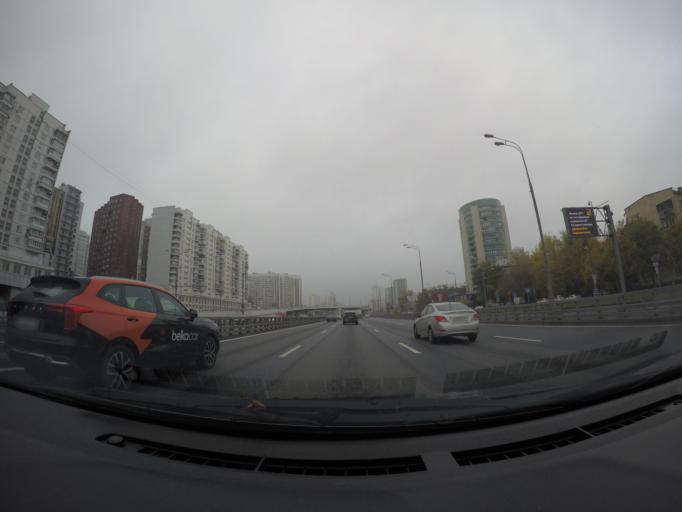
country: RU
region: Moskovskaya
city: Khoroshevo-Mnevniki
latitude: 55.7757
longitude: 37.4742
